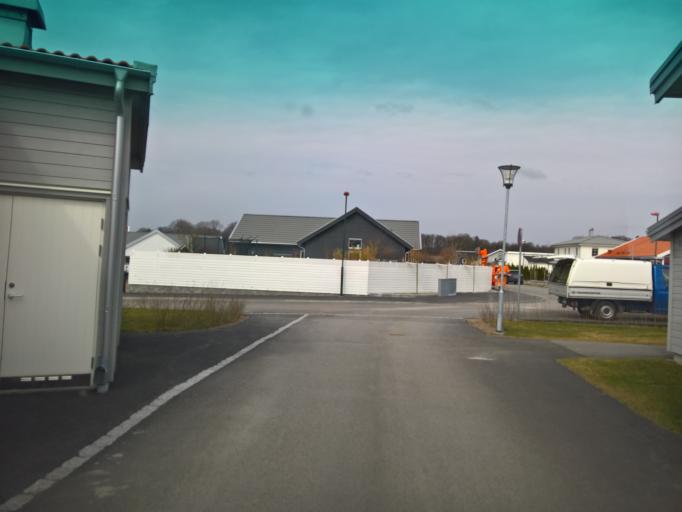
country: SE
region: Skane
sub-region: Hoors Kommun
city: Hoeoer
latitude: 55.9438
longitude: 13.5336
